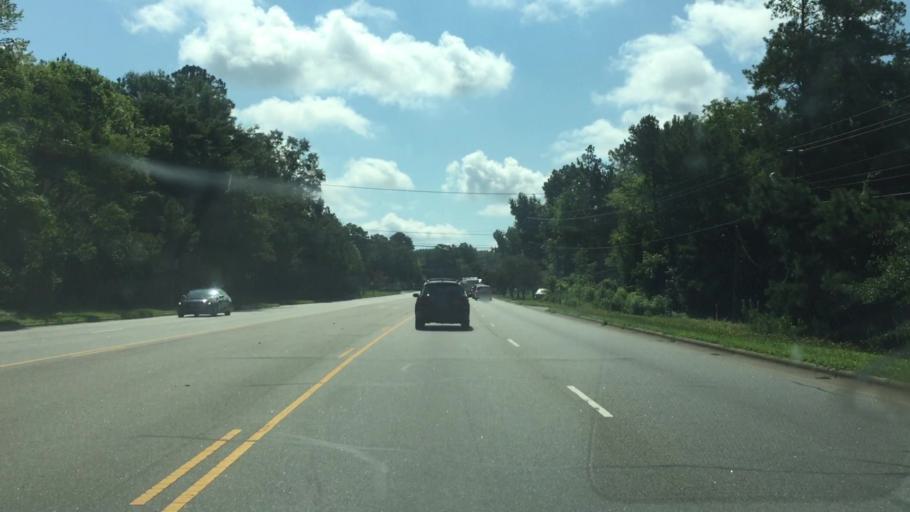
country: US
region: North Carolina
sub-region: Anson County
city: Wadesboro
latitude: 34.9773
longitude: -80.0887
